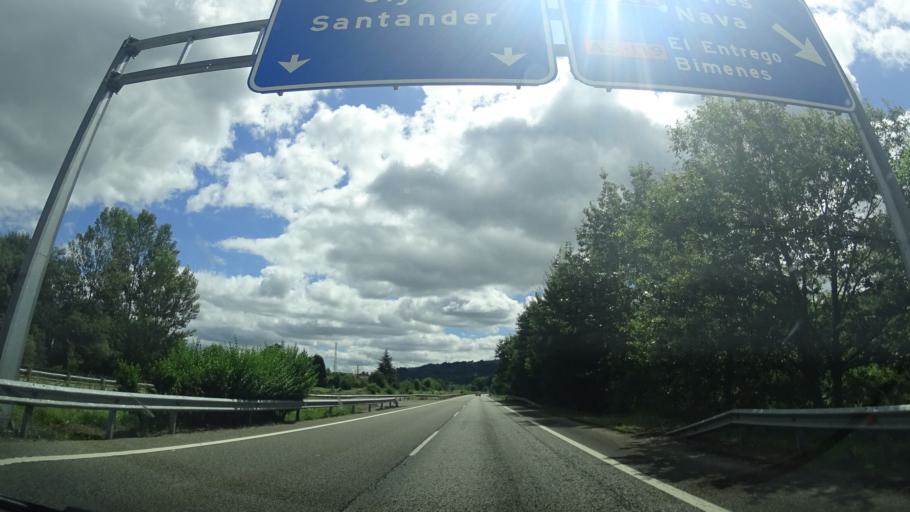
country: ES
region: Asturias
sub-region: Province of Asturias
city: Pola de Siero
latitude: 43.3819
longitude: -5.6141
